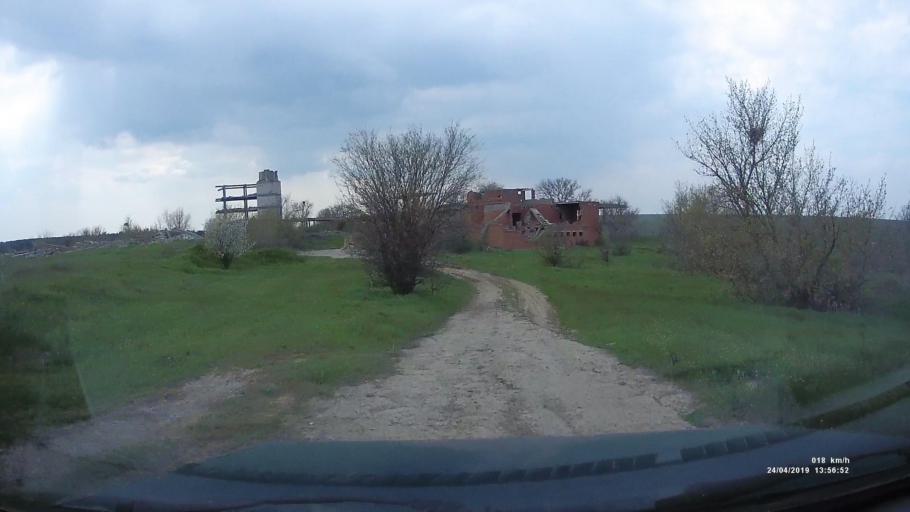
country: RU
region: Kalmykiya
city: Arshan'
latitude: 46.2634
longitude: 44.2174
